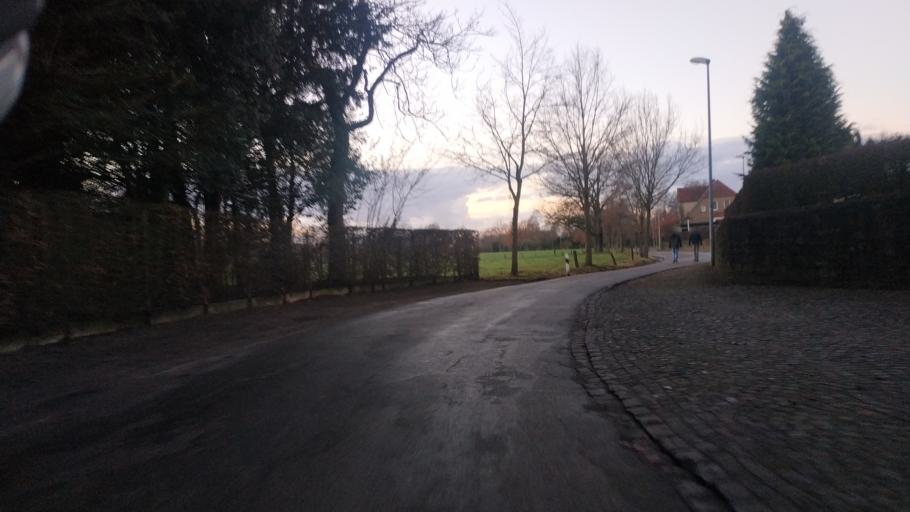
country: DE
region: North Rhine-Westphalia
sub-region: Regierungsbezirk Munster
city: Mettingen
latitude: 52.3168
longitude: 7.7713
